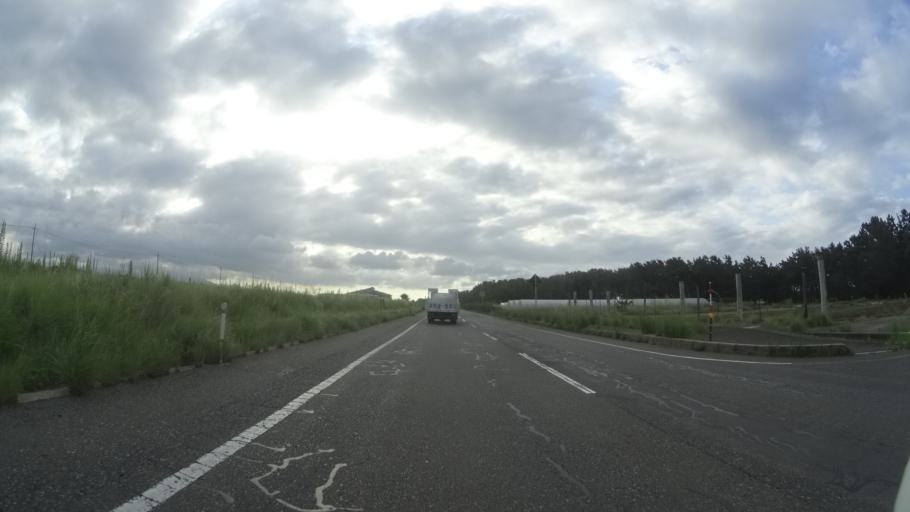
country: JP
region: Tottori
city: Kurayoshi
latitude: 35.4989
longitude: 133.7696
